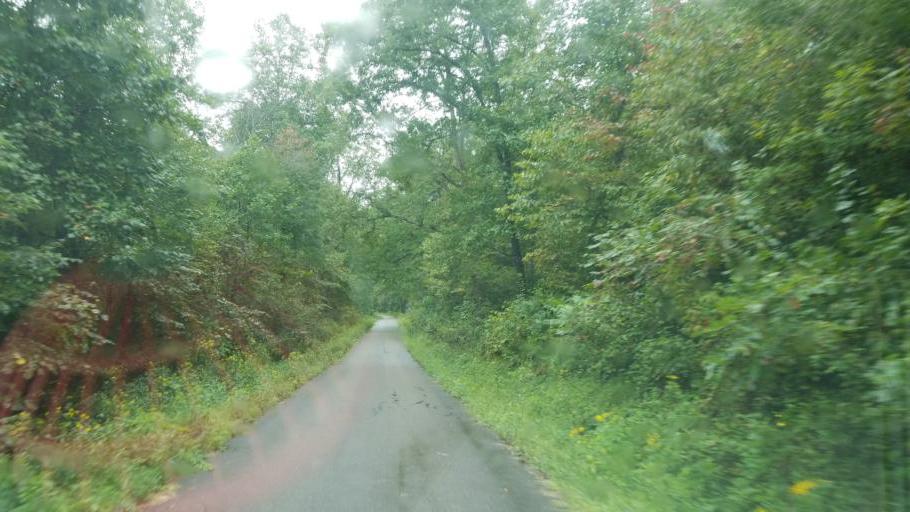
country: US
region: Ohio
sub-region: Scioto County
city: West Portsmouth
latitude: 38.7755
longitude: -83.1458
